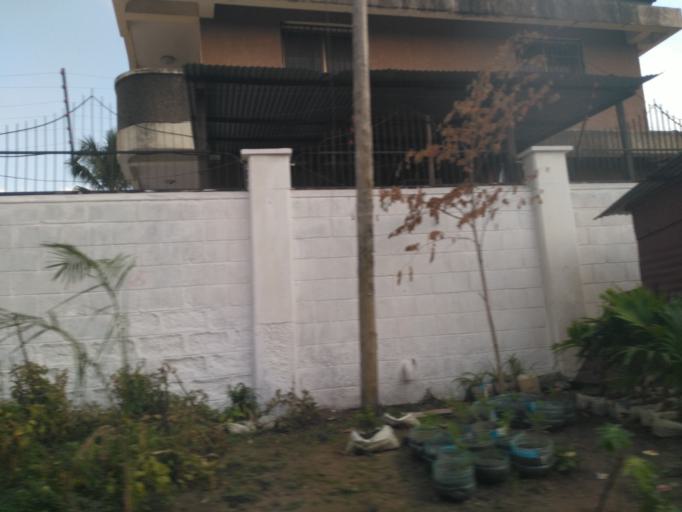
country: TZ
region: Dar es Salaam
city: Magomeni
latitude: -6.7427
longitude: 39.2389
